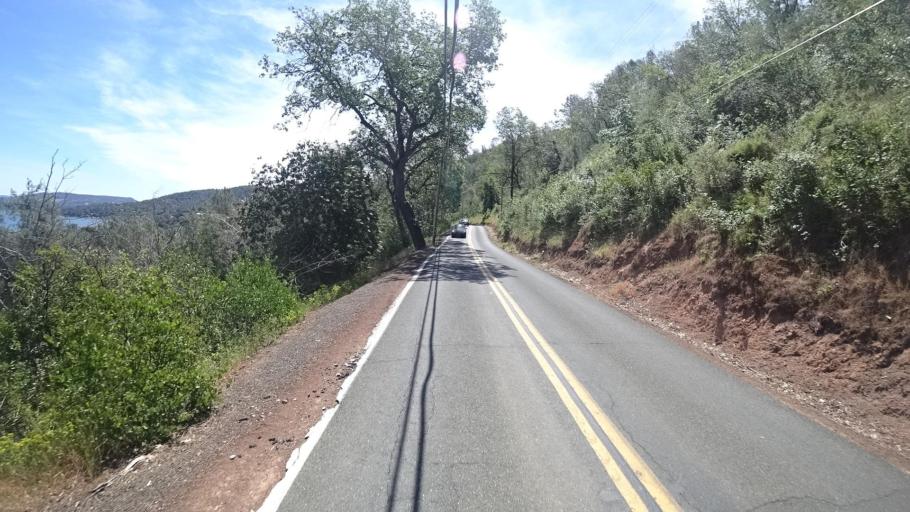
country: US
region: California
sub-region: Lake County
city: Clearlake
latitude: 38.9448
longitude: -122.6801
